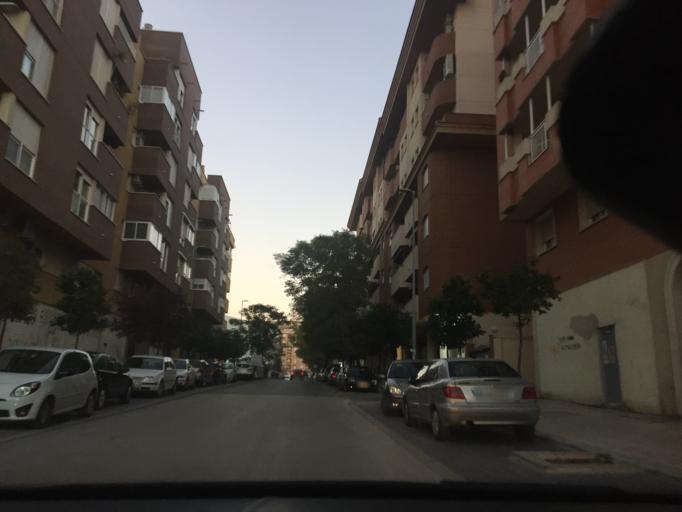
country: ES
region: Andalusia
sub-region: Provincia de Jaen
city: Jaen
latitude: 37.7829
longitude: -3.7891
